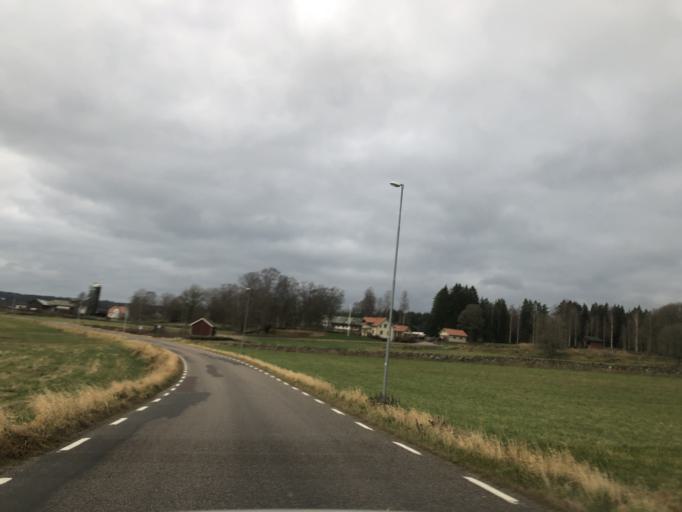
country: SE
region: Vaestra Goetaland
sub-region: Boras Kommun
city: Dalsjofors
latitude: 57.8291
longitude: 13.1748
